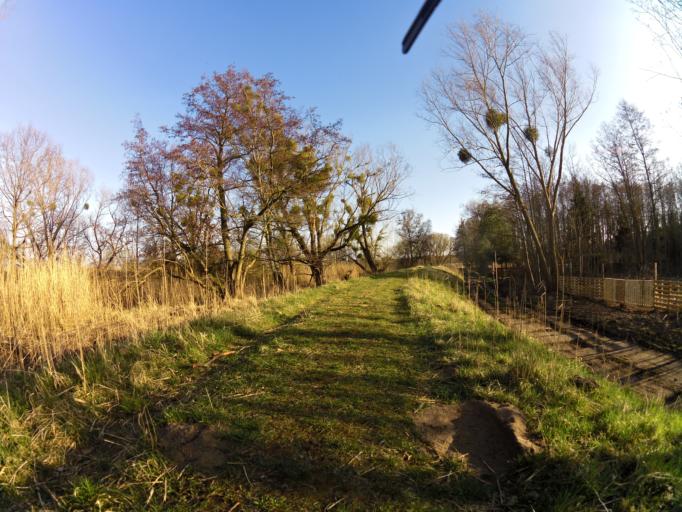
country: PL
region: West Pomeranian Voivodeship
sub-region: Powiat policki
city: Nowe Warpno
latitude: 53.7289
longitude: 14.3331
